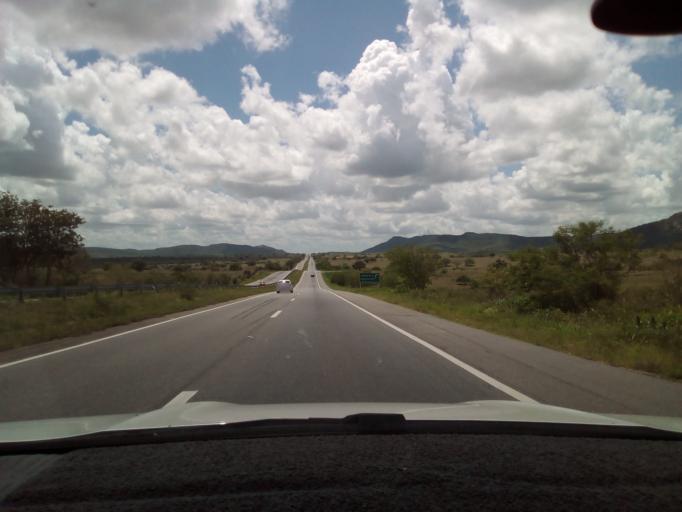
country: BR
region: Paraiba
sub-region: Gurinhem
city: Gurinhem
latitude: -7.1912
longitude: -35.4715
